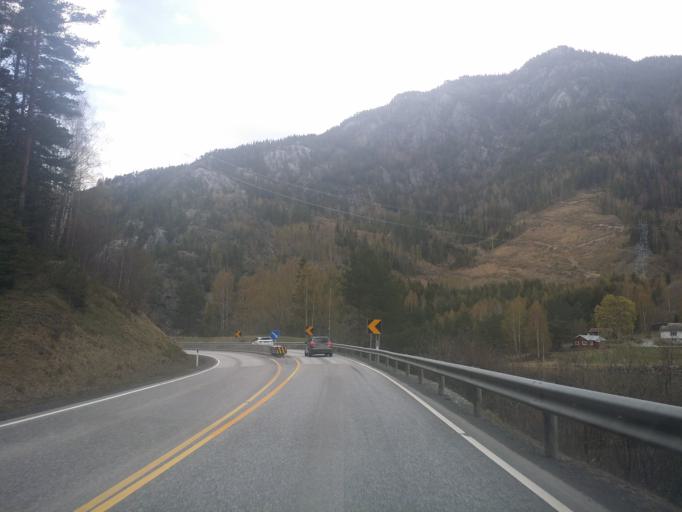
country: NO
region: Buskerud
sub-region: Nes
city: Nesbyen
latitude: 60.4863
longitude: 9.2216
